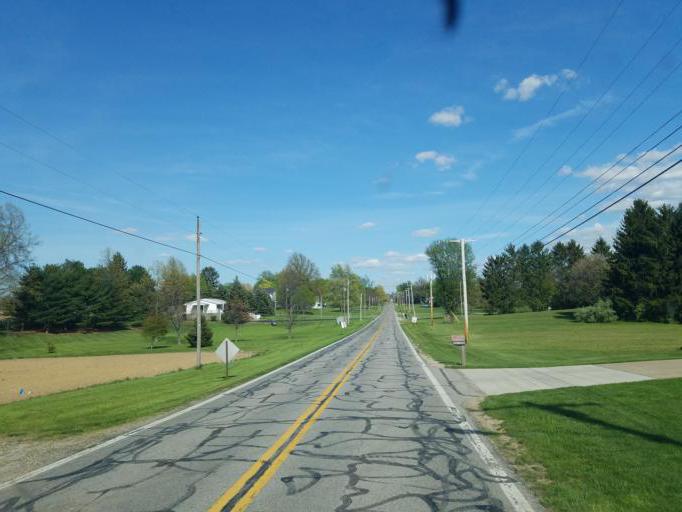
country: US
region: Ohio
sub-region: Huron County
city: Plymouth
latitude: 40.9953
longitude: -82.6838
